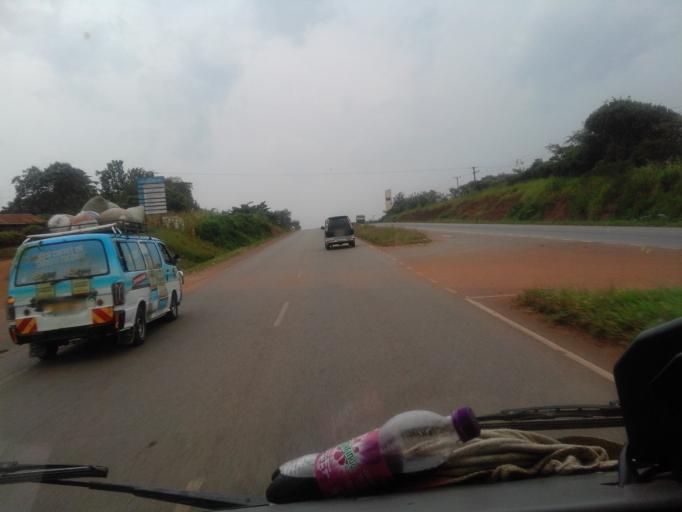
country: UG
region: Eastern Region
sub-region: Jinja District
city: Bugembe
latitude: 0.4777
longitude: 33.2688
